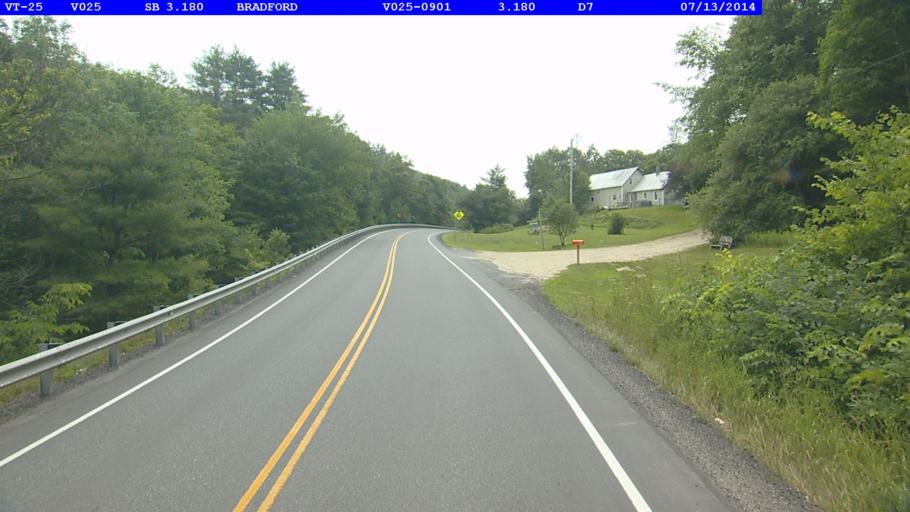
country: US
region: New Hampshire
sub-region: Grafton County
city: Orford
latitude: 44.0007
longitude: -72.1612
